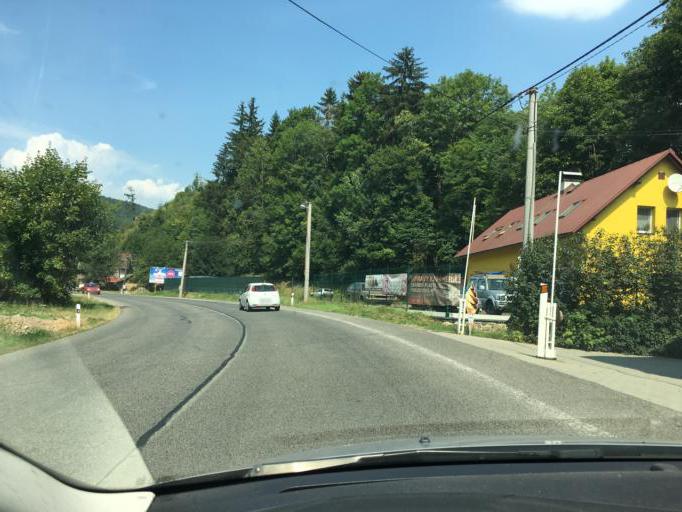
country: CZ
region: Liberecky
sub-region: Okres Semily
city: Ponikla
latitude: 50.6496
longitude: 15.4588
